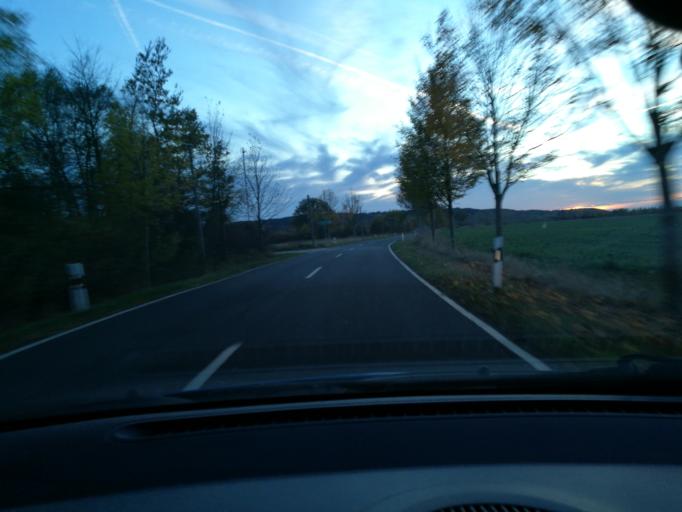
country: DE
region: Brandenburg
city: Lenzen
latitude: 53.0829
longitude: 11.4616
